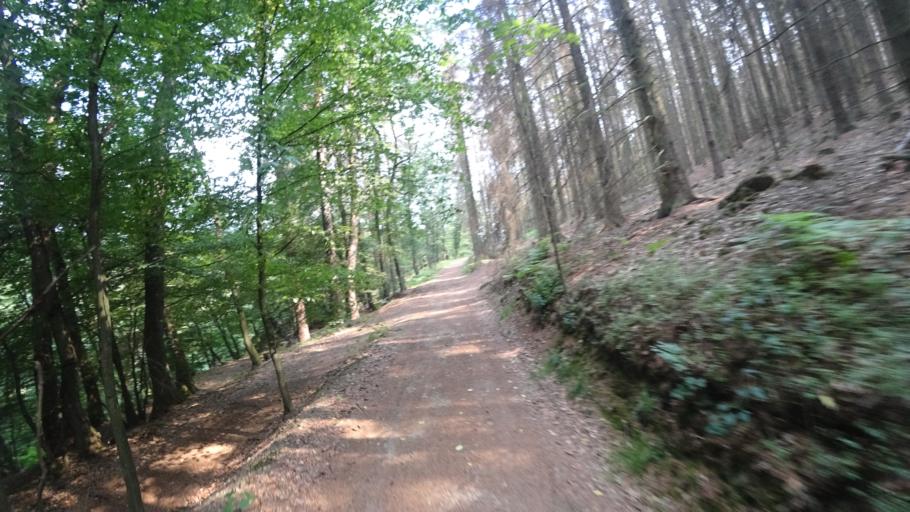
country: DE
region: Rheinland-Pfalz
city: Wirscheid
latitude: 50.4598
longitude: 7.6688
